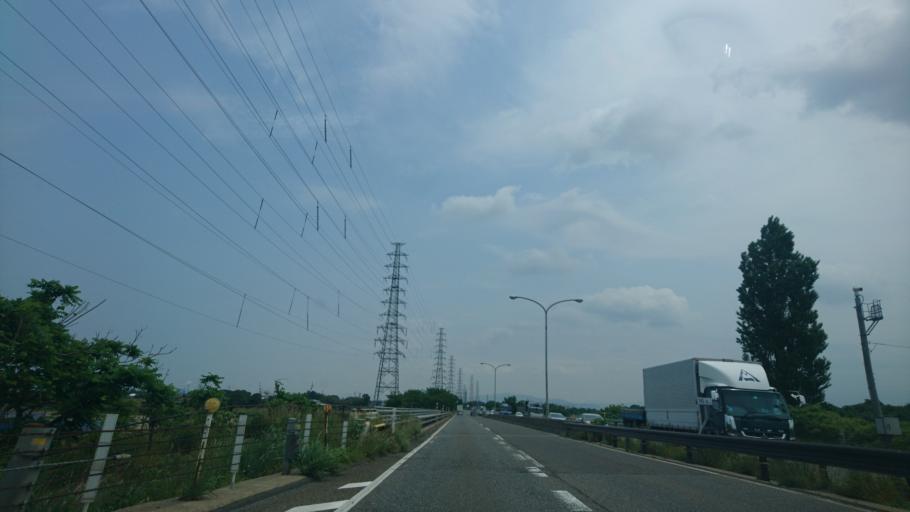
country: JP
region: Niigata
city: Suibara
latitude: 37.9474
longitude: 139.1965
